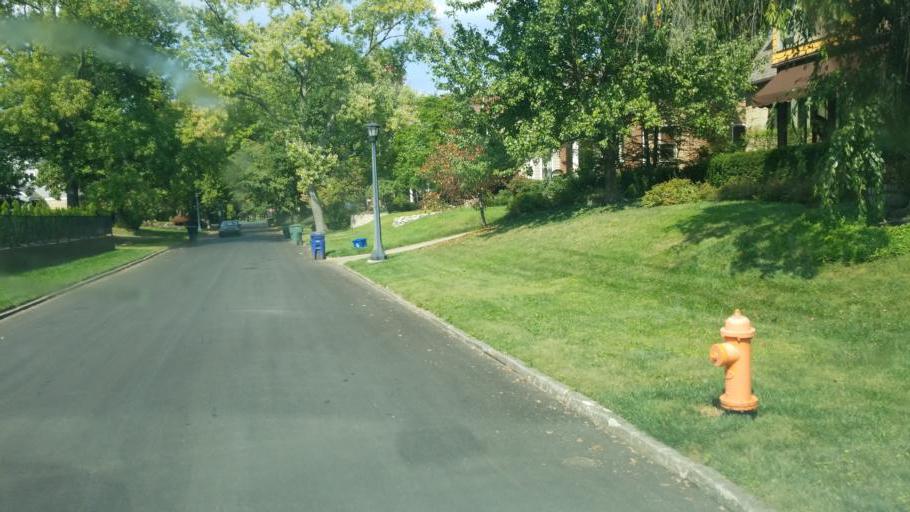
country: US
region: Ohio
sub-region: Franklin County
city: Worthington
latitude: 40.0347
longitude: -83.0190
